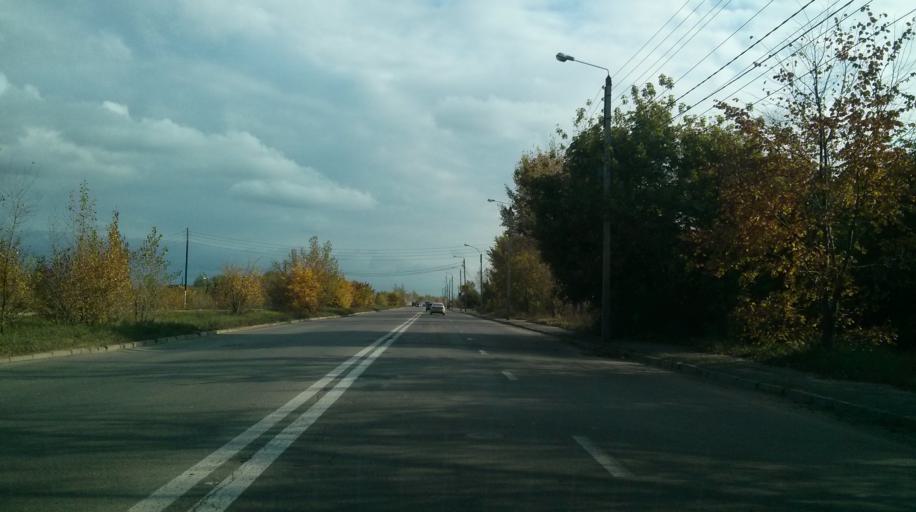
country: RU
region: Nizjnij Novgorod
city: Bor
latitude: 56.3133
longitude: 44.0870
